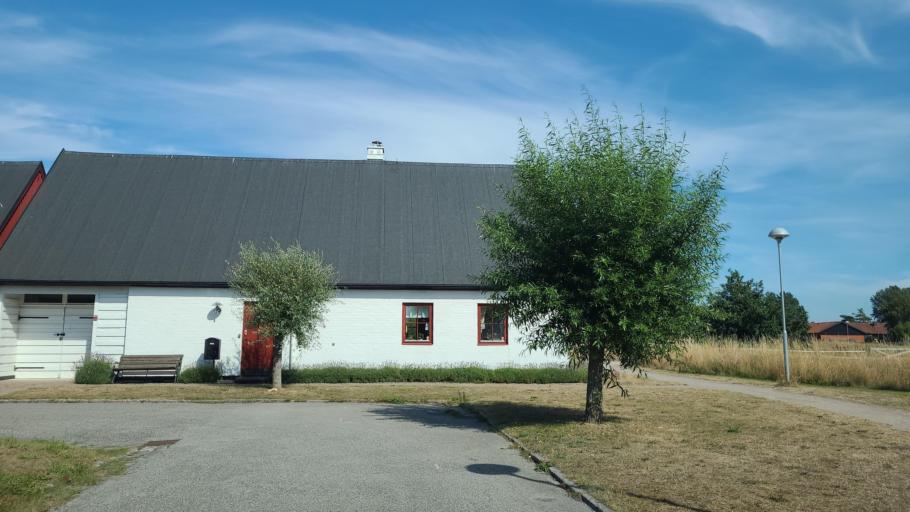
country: SE
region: Skane
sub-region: Vellinge Kommun
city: Skanor med Falsterbo
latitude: 55.4189
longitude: 12.8580
